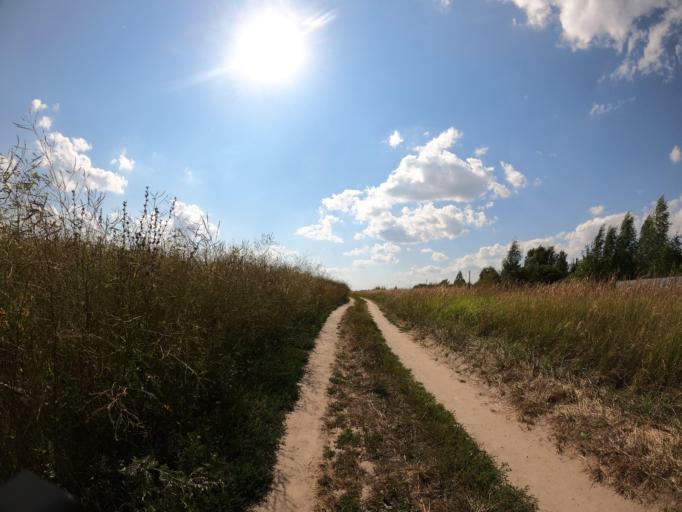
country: RU
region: Moskovskaya
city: Peski
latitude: 55.2321
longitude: 38.7587
